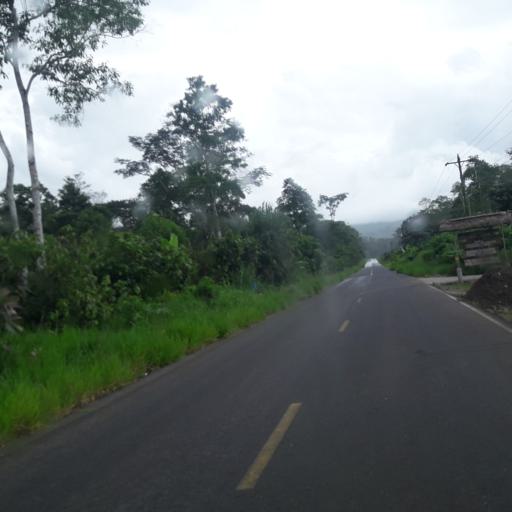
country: EC
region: Napo
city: Tena
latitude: -1.0456
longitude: -77.6638
